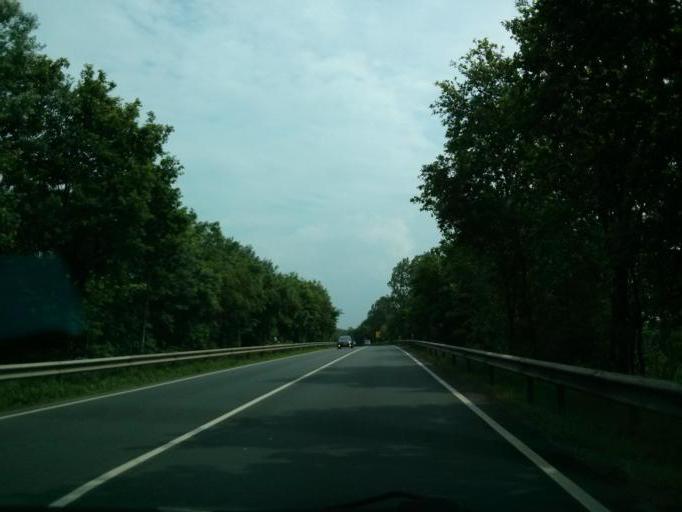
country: DE
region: Lower Saxony
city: Loxstedt
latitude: 53.4945
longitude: 8.6347
